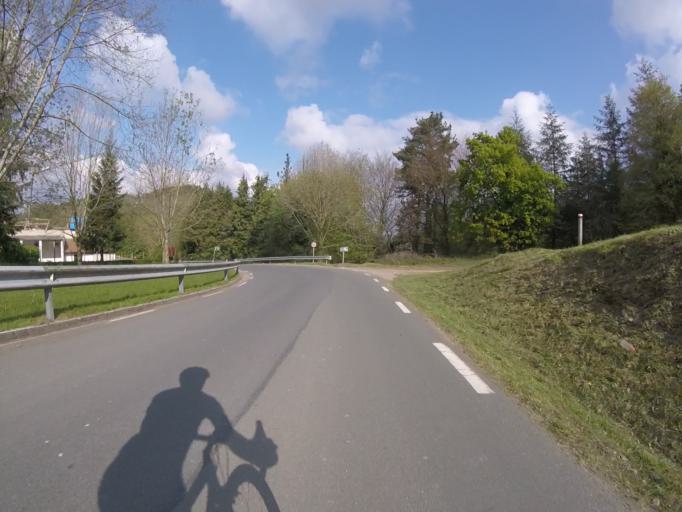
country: ES
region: Basque Country
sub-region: Provincia de Guipuzcoa
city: Azkoitia
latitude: 43.2081
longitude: -2.3433
